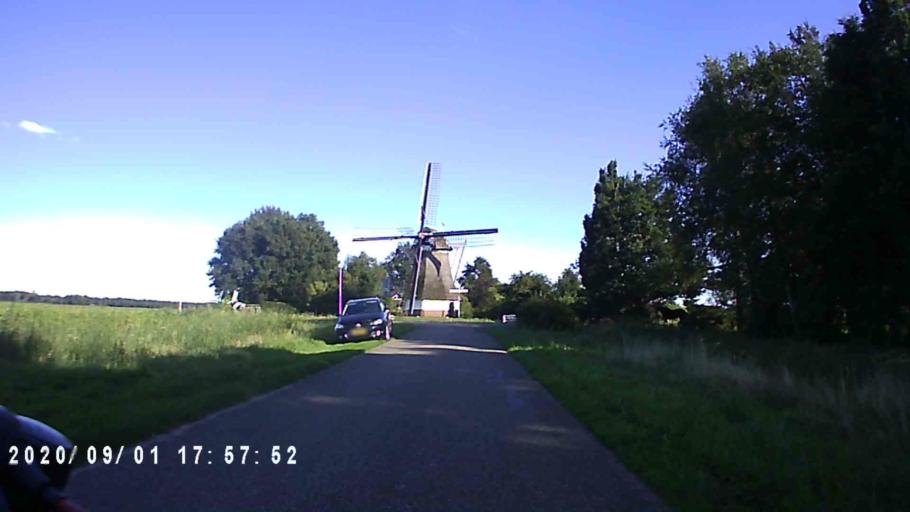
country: NL
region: Groningen
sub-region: Gemeente Slochteren
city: Slochteren
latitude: 53.2064
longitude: 6.7708
